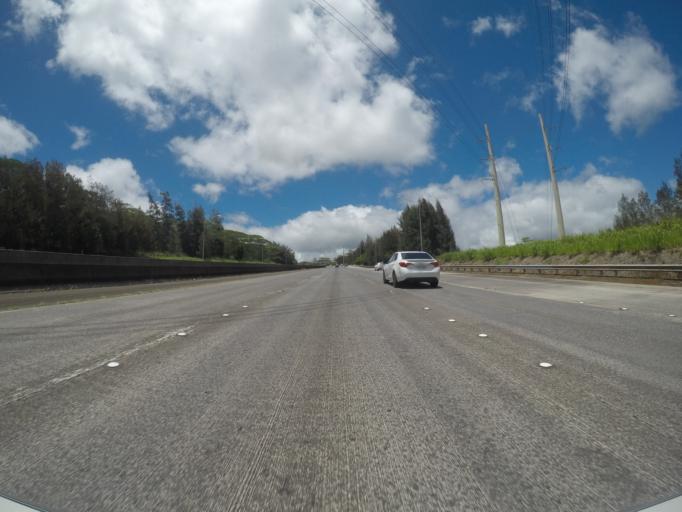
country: US
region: Hawaii
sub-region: Honolulu County
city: Mililani Town
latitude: 21.4436
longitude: -157.9927
